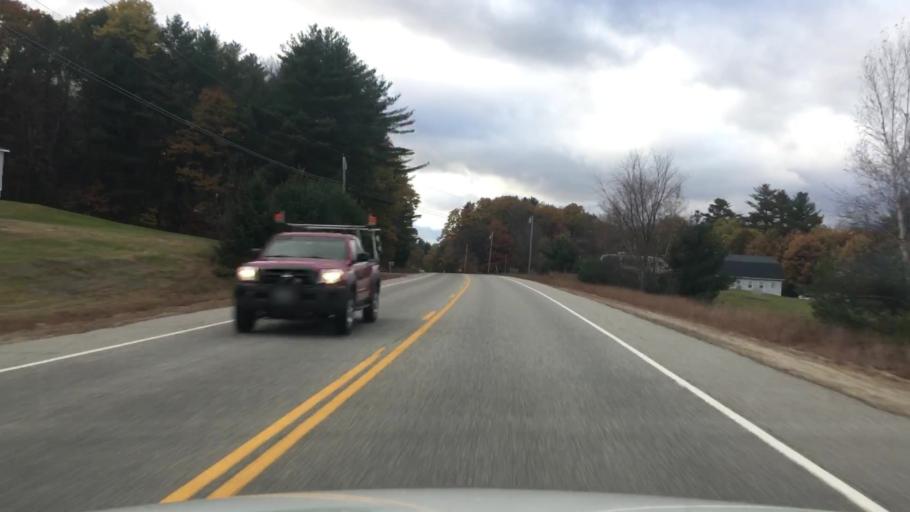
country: US
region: Maine
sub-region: Androscoggin County
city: Livermore
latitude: 44.4133
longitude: -70.2821
